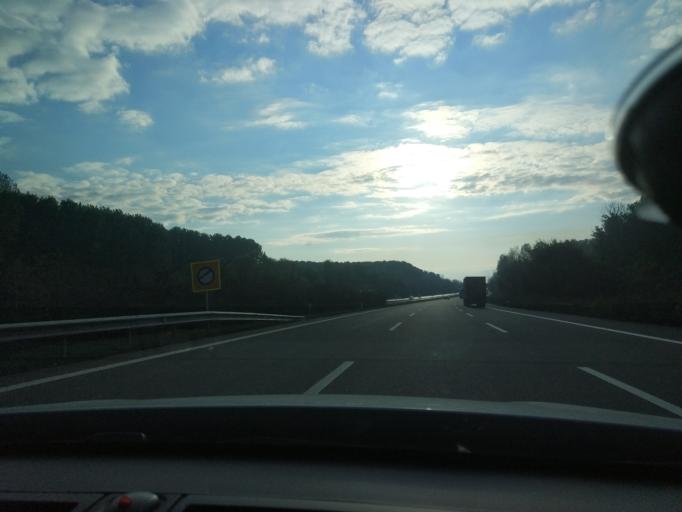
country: TR
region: Duzce
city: Duzce
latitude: 40.8103
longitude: 31.1405
